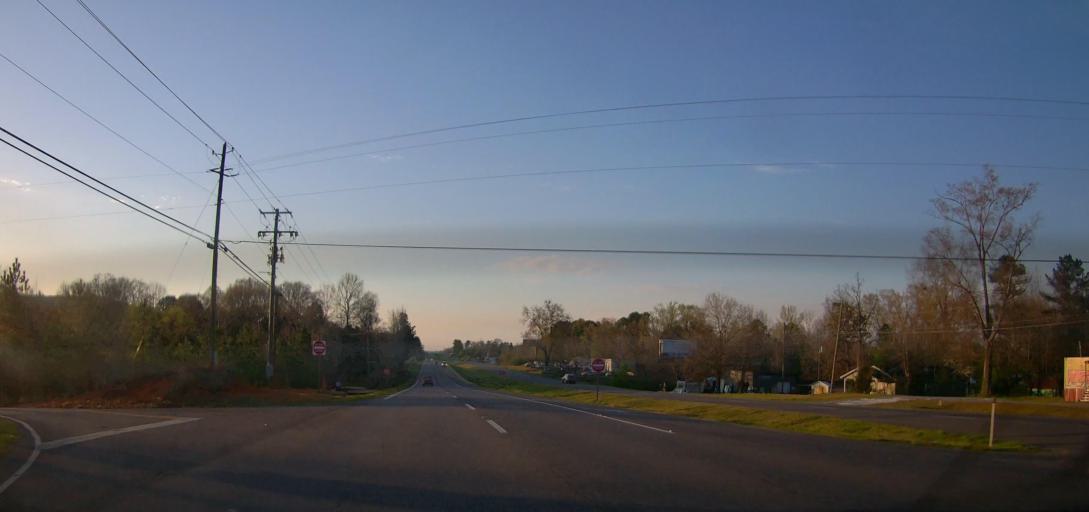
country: US
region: Alabama
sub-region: Talladega County
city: Childersburg
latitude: 33.2477
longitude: -86.3388
